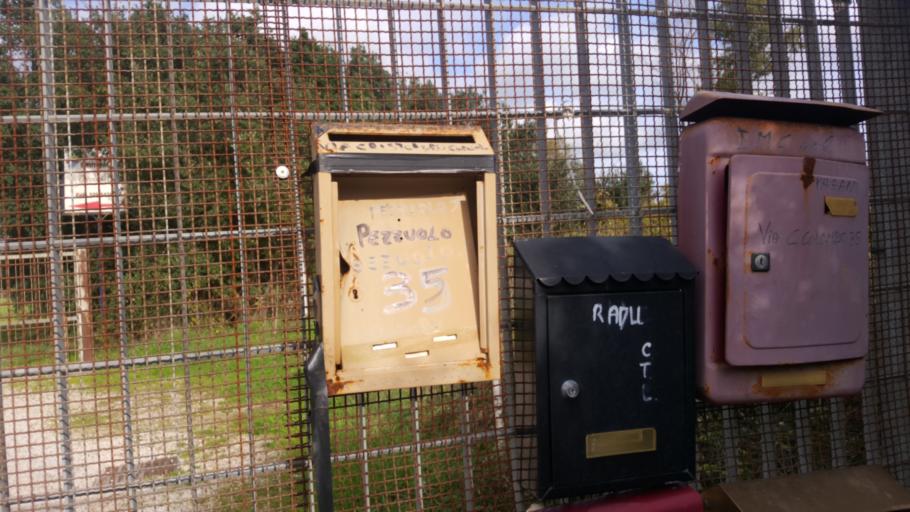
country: IT
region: Latium
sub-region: Provincia di Latina
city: Latina
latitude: 41.4767
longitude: 12.8863
